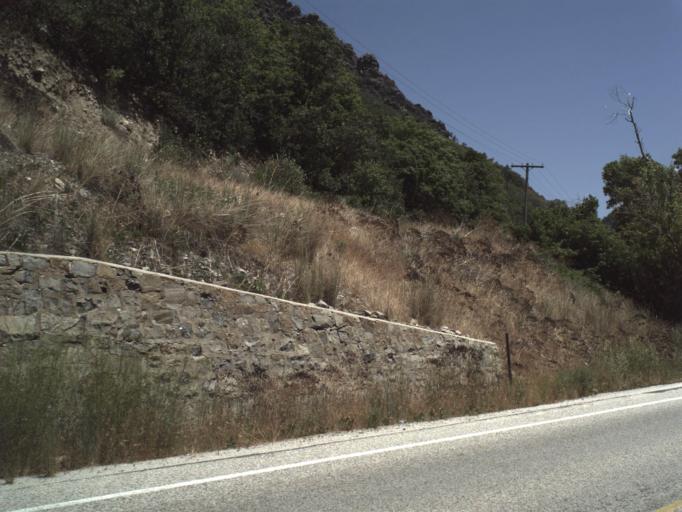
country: US
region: Utah
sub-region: Weber County
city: Liberty
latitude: 41.2546
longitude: -111.8580
